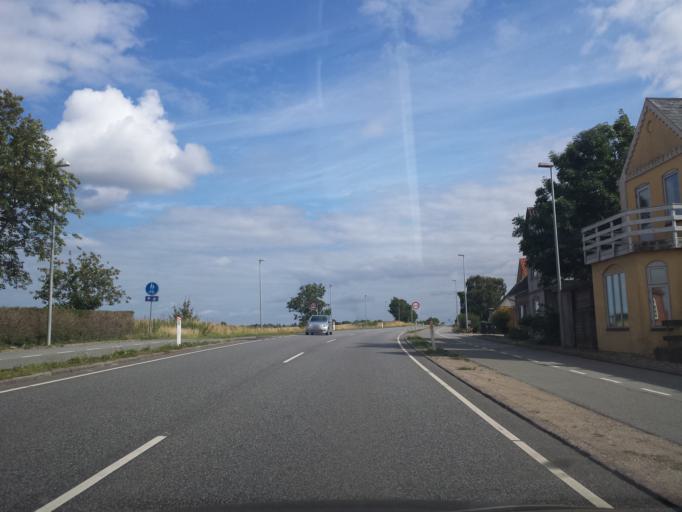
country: DK
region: South Denmark
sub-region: Sonderborg Kommune
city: Guderup
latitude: 55.0267
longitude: 9.8348
